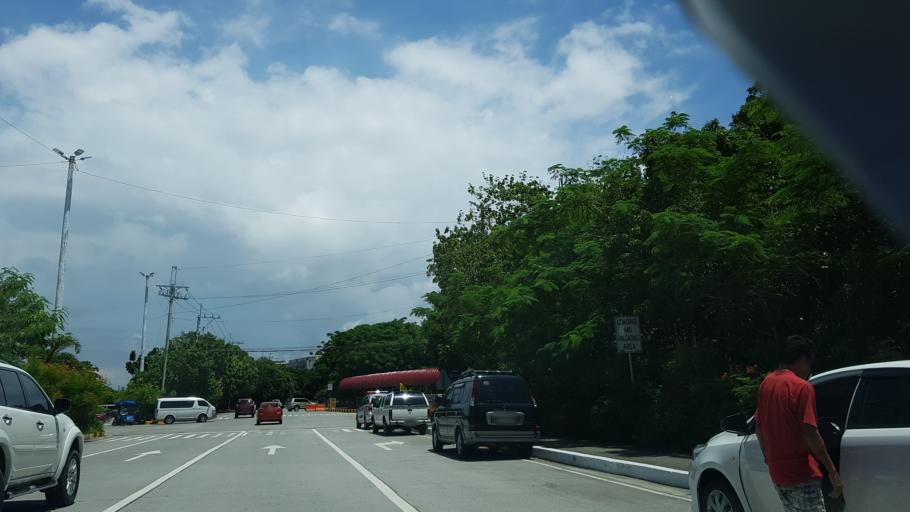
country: PH
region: Metro Manila
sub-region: City of Manila
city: Port Area
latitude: 14.5454
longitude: 120.9823
